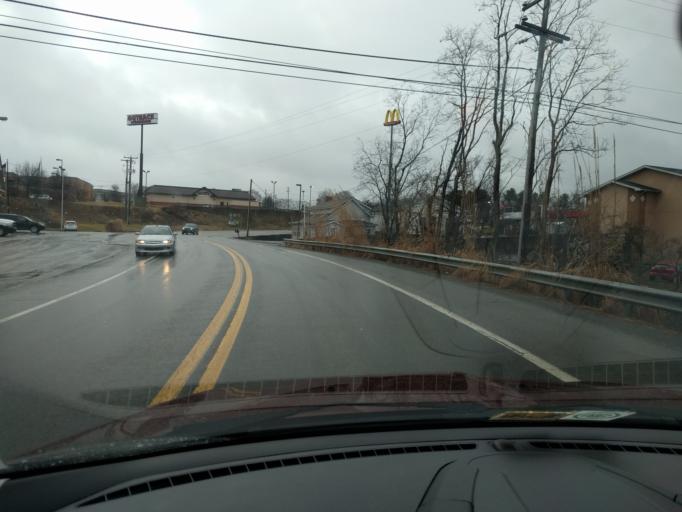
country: US
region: West Virginia
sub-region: Raleigh County
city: Mabscott
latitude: 37.7933
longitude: -81.2146
